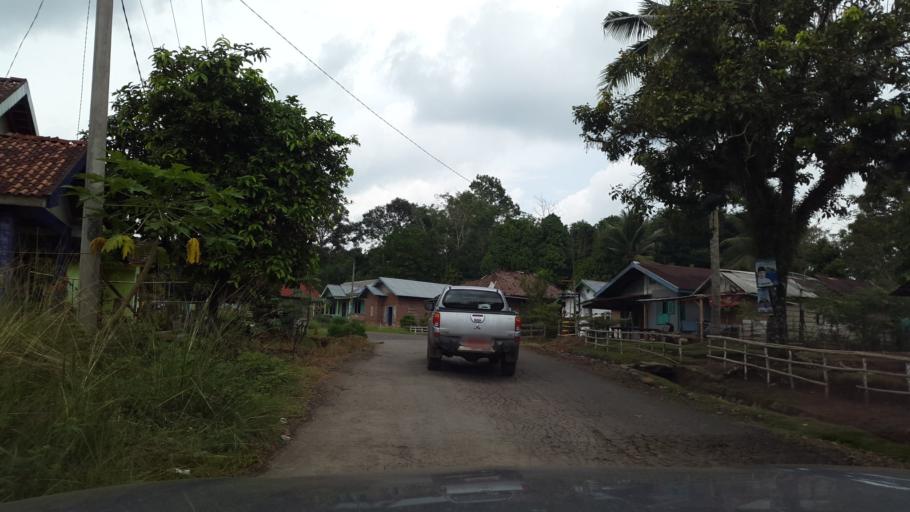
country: ID
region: South Sumatra
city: Terawas
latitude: -3.0890
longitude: 102.9040
